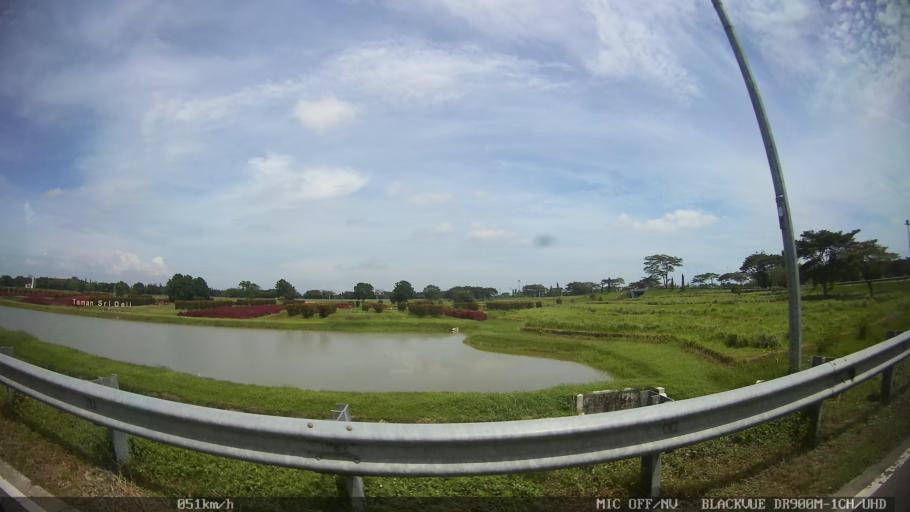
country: ID
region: North Sumatra
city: Percut
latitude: 3.6306
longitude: 98.8765
